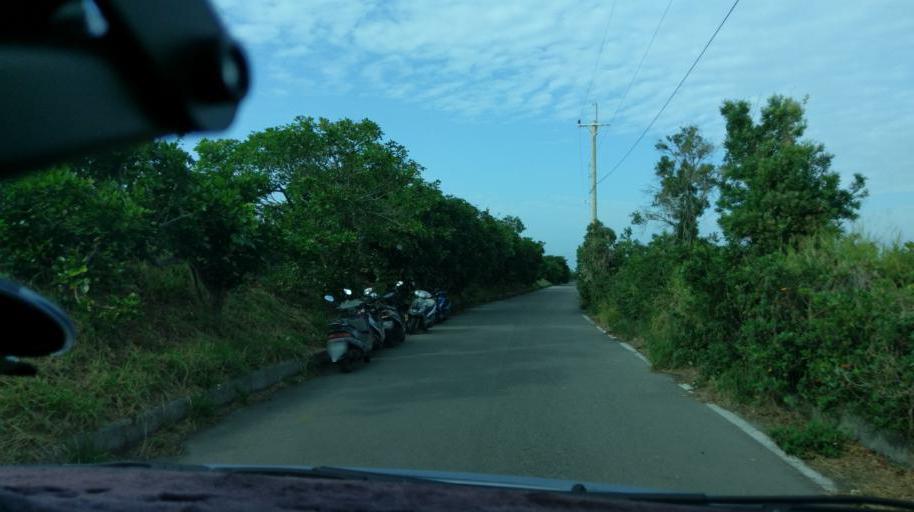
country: TW
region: Taiwan
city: Fengyuan
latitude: 24.3162
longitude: 120.5510
